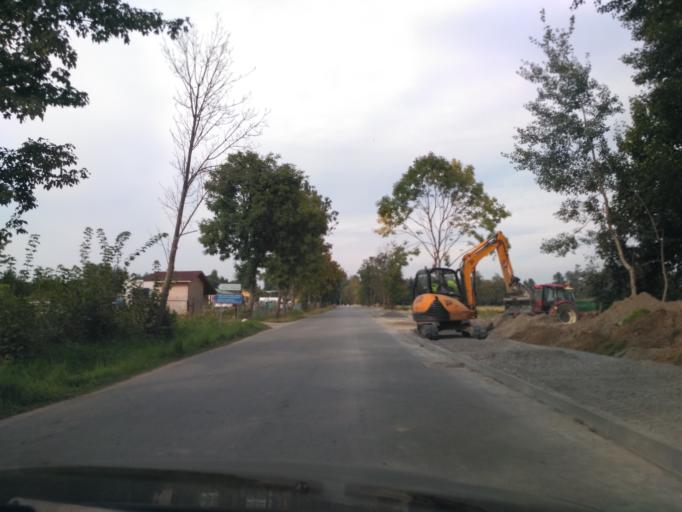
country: PL
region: Subcarpathian Voivodeship
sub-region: Powiat rzeszowski
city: Swilcza
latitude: 50.0886
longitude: 21.9164
